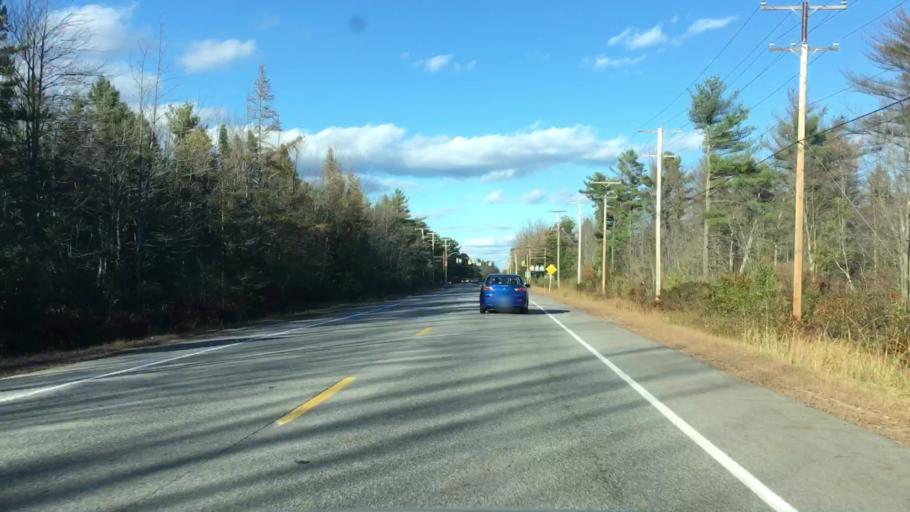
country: US
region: Maine
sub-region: Cumberland County
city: West Scarborough
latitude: 43.6067
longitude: -70.3632
